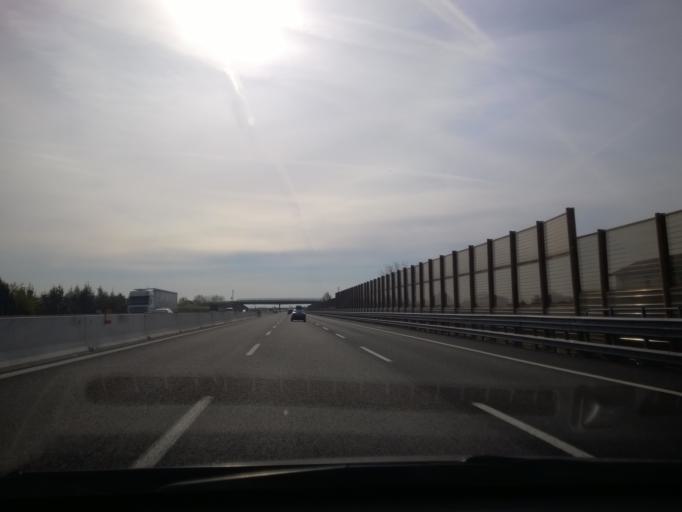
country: IT
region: Emilia-Romagna
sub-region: Forli-Cesena
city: Cesena
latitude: 44.1875
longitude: 12.2436
